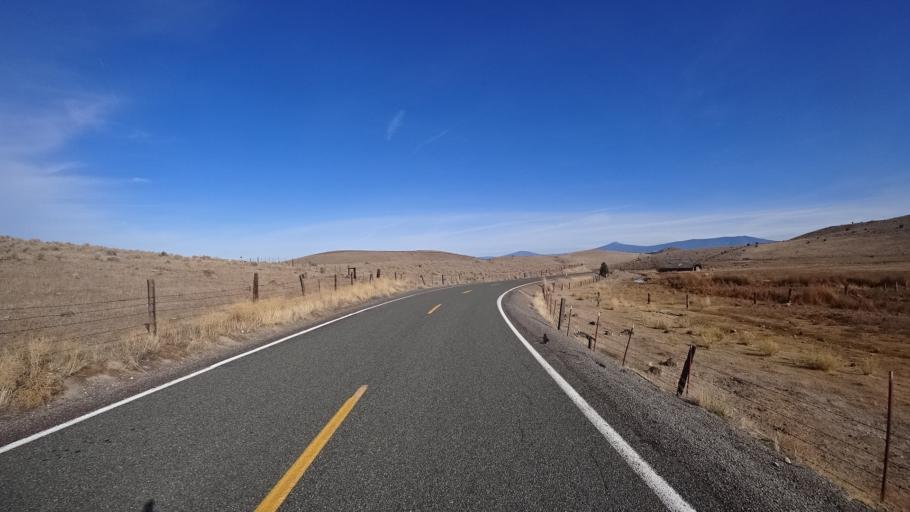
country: US
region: California
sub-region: Siskiyou County
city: Weed
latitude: 41.5485
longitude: -122.4964
